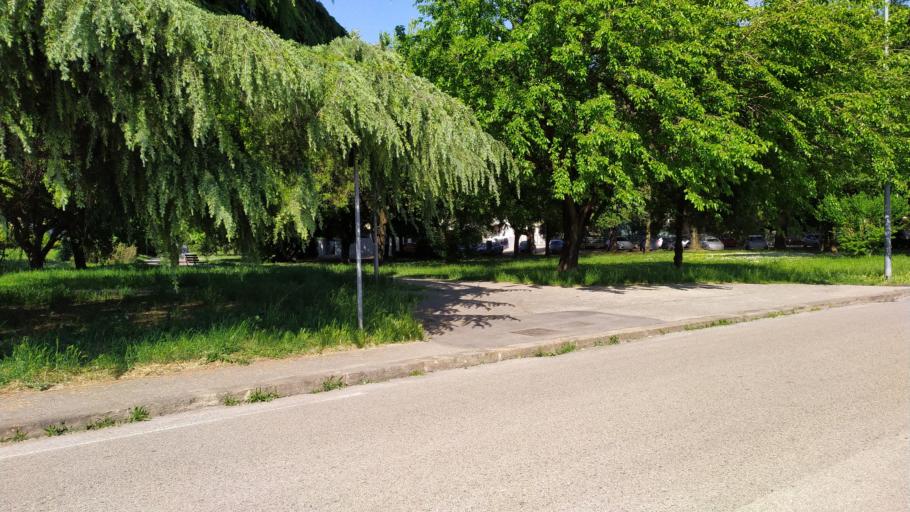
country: IT
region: Veneto
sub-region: Provincia di Vicenza
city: Vicenza
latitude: 45.5478
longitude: 11.5230
